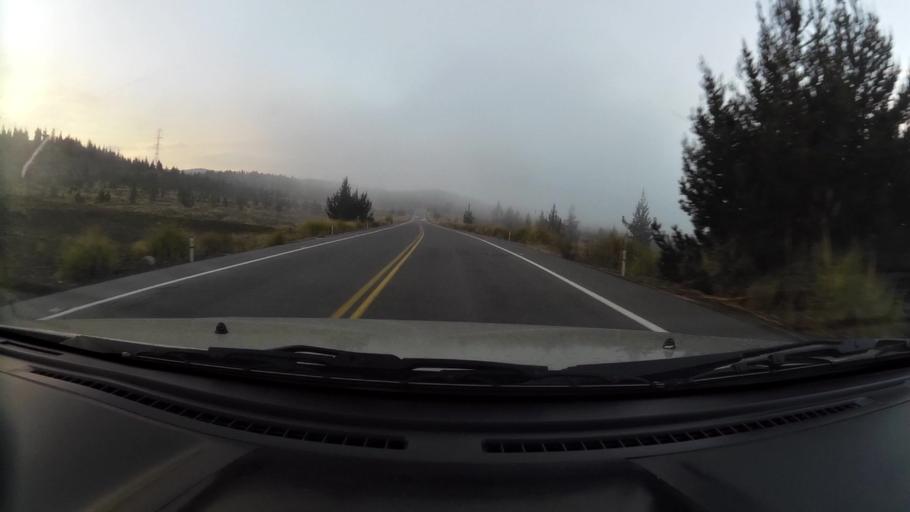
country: EC
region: Chimborazo
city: Alausi
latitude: -2.0533
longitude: -78.7432
